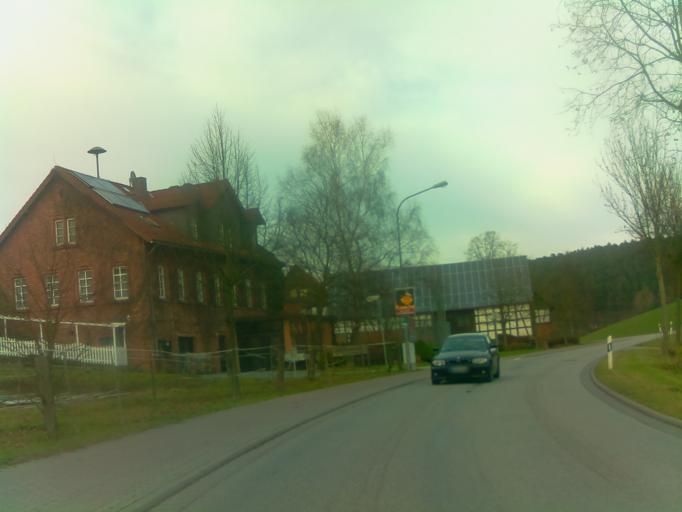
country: DE
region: Hesse
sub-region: Regierungsbezirk Darmstadt
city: Erbach
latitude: 49.6518
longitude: 8.9298
